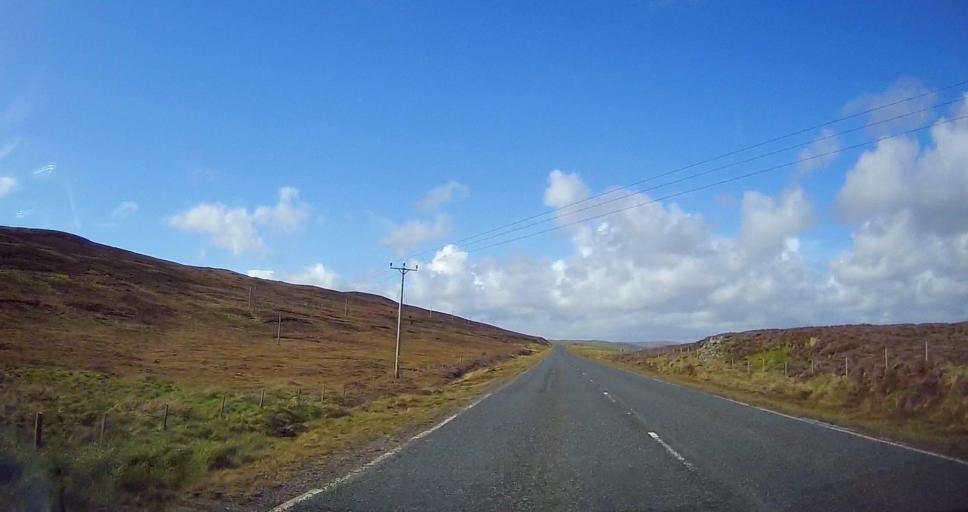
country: GB
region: Scotland
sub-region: Shetland Islands
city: Lerwick
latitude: 60.2103
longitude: -1.2335
